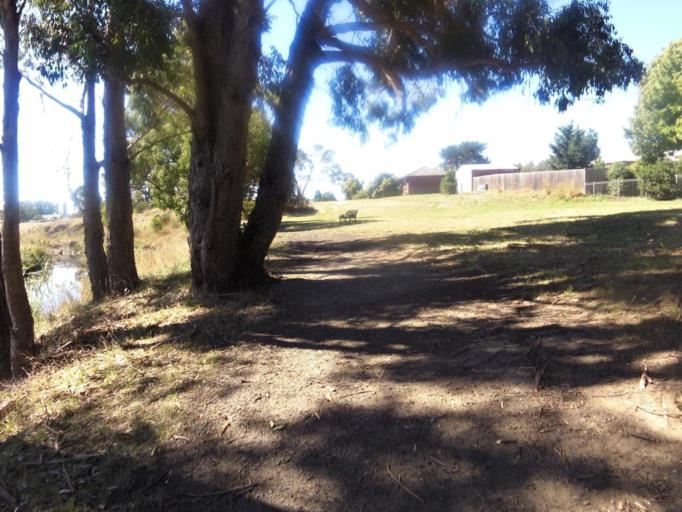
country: AU
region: Victoria
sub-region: Mount Alexander
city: Castlemaine
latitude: -37.2477
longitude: 144.4422
